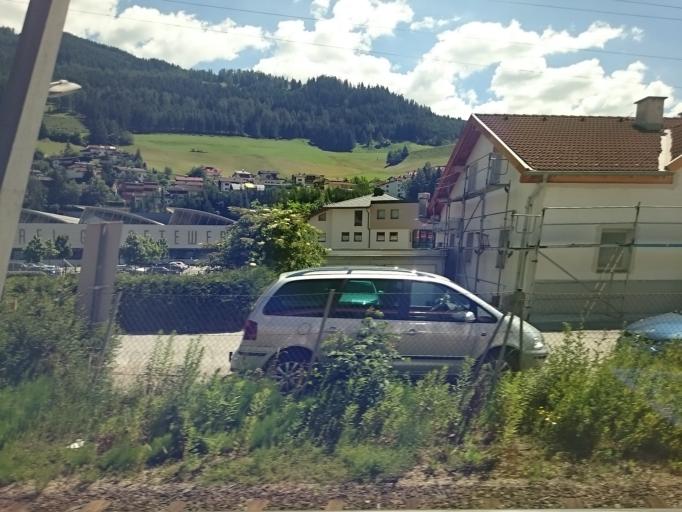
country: AT
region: Tyrol
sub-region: Politischer Bezirk Innsbruck Land
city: Matrei am Brenner
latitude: 47.1261
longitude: 11.4523
